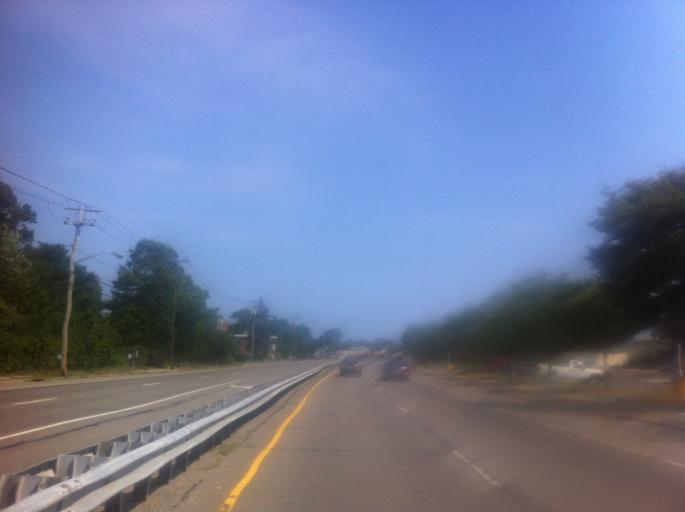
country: US
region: New York
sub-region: Suffolk County
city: West Babylon
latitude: 40.7056
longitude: -73.3471
